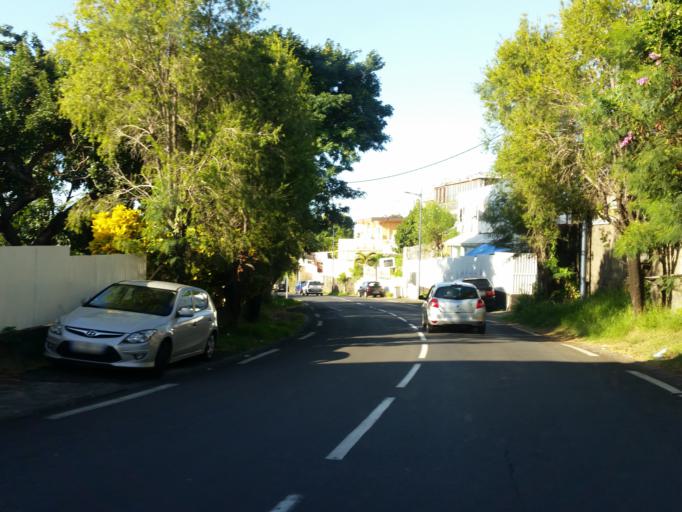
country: RE
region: Reunion
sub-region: Reunion
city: Saint-Denis
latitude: -20.8992
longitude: 55.4602
